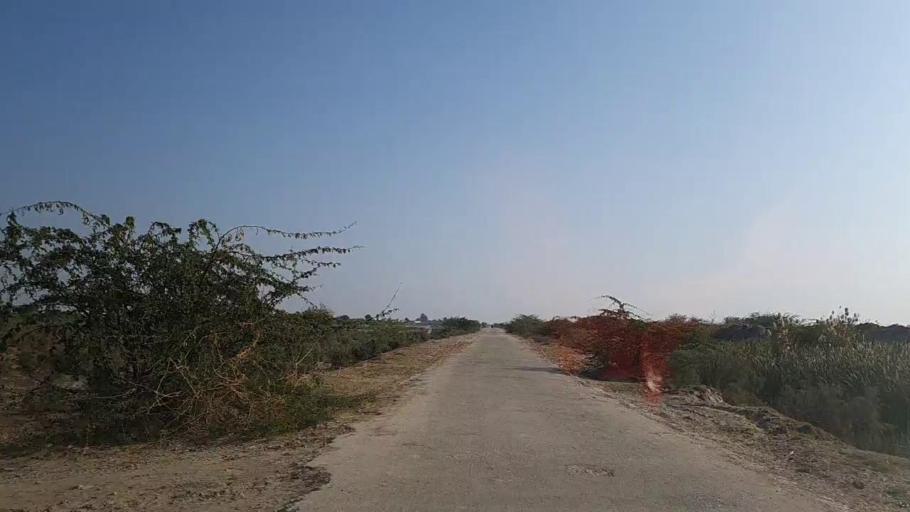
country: PK
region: Sindh
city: Tando Mittha Khan
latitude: 25.9362
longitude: 69.0583
